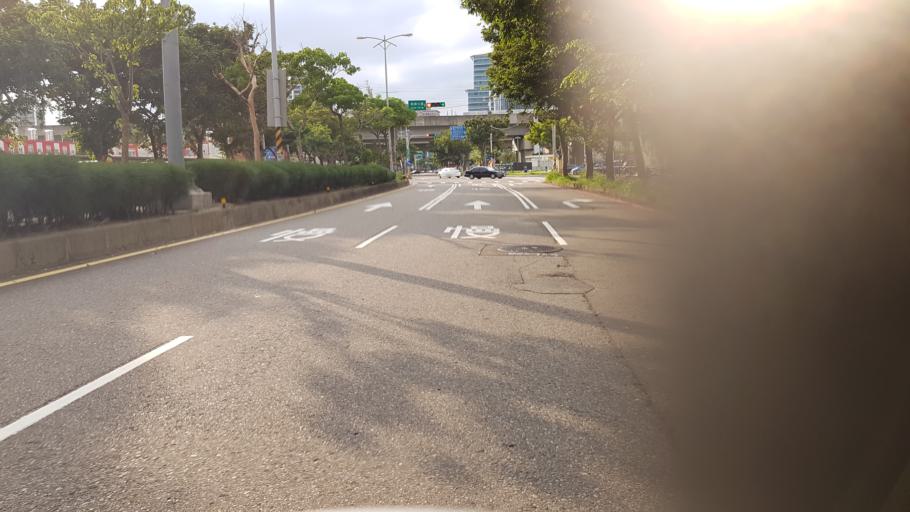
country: TW
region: Taiwan
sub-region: Hsinchu
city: Zhubei
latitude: 24.8057
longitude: 121.0417
